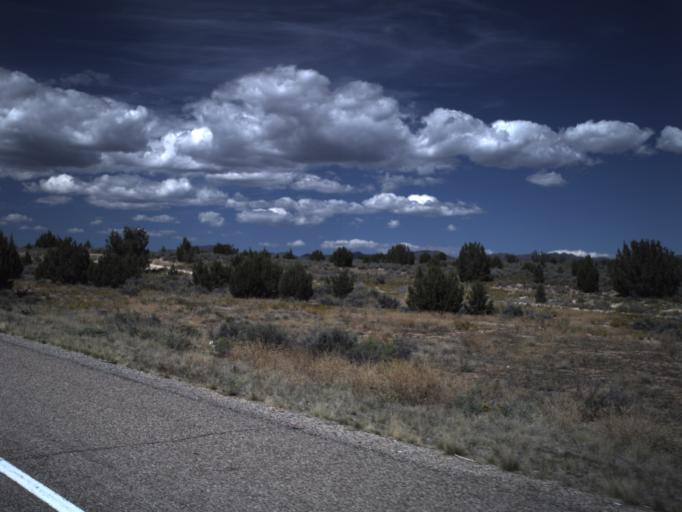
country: US
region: Utah
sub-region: Washington County
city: Ivins
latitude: 37.3186
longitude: -113.6815
